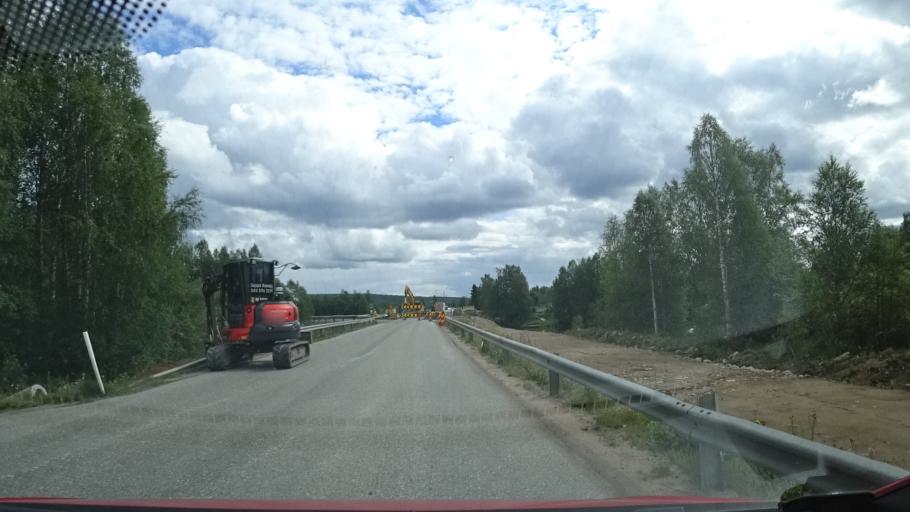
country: FI
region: Lapland
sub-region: Rovaniemi
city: Rovaniemi
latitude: 66.5249
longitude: 25.7440
